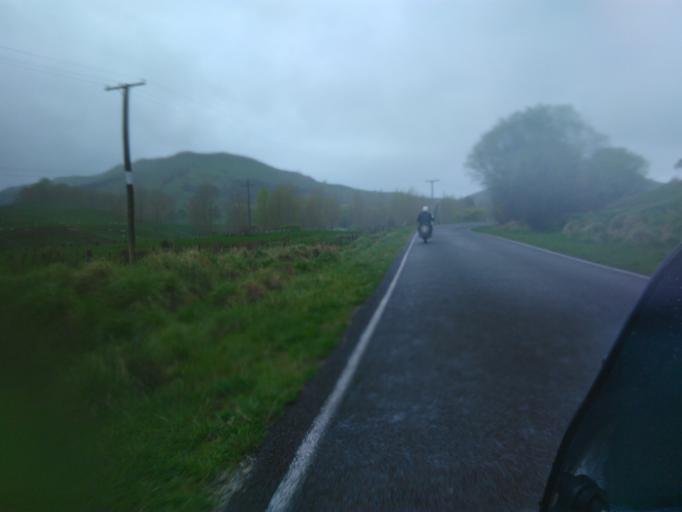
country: NZ
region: Gisborne
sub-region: Gisborne District
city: Gisborne
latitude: -38.6770
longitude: 177.7223
